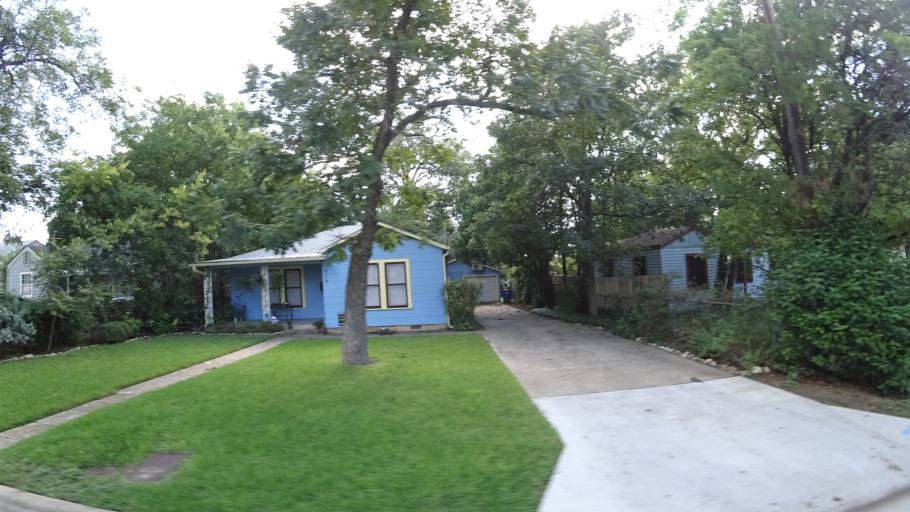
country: US
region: Texas
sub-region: Travis County
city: Austin
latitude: 30.3085
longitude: -97.7142
